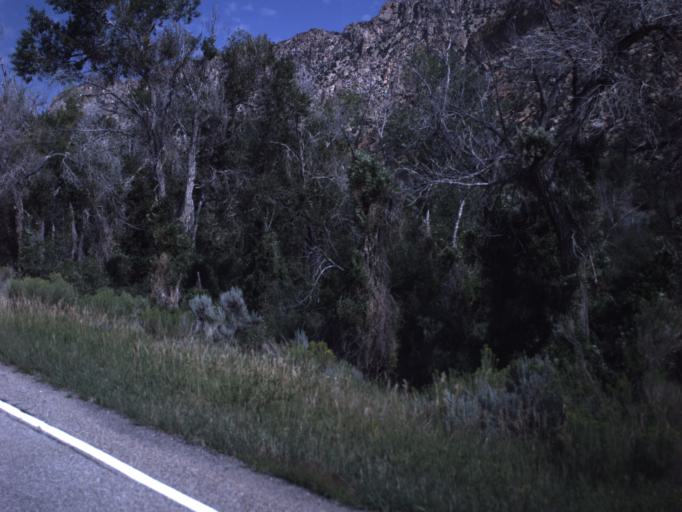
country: US
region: Utah
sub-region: Daggett County
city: Manila
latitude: 40.9204
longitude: -109.6999
